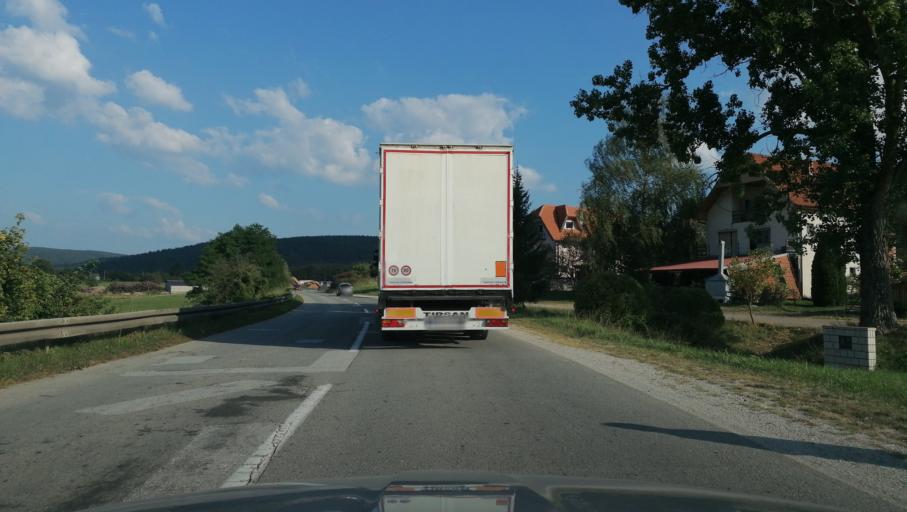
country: RS
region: Central Serbia
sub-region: Zlatiborski Okrug
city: Bajina Basta
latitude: 43.8444
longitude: 19.5950
